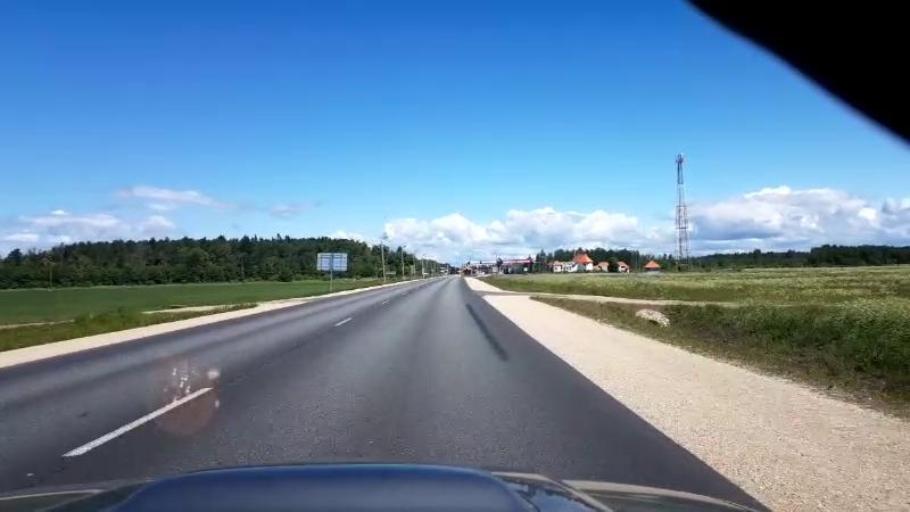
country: LV
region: Salacgrivas
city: Ainazi
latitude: 57.8719
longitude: 24.3784
